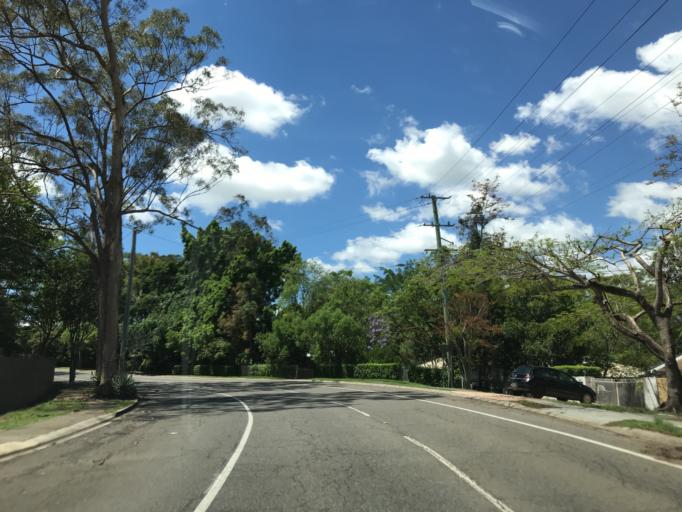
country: AU
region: Queensland
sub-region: Brisbane
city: Kenmore Hills
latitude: -27.5242
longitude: 152.9477
